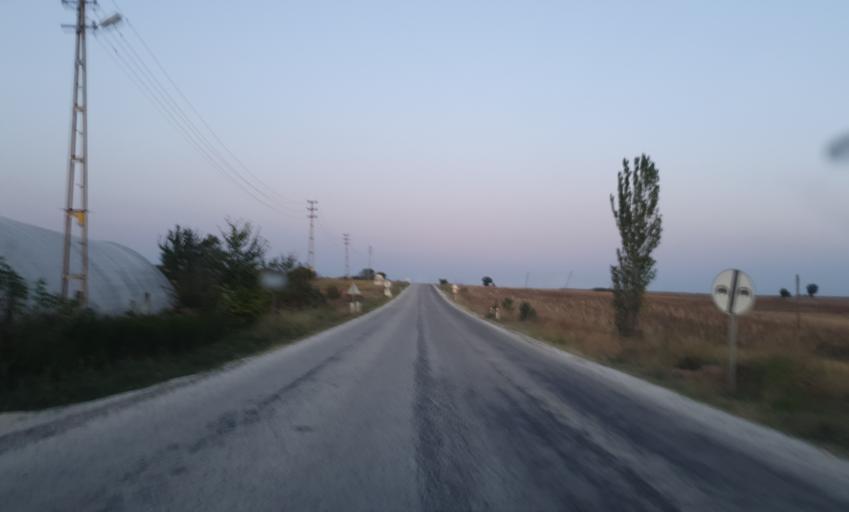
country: TR
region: Kirklareli
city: Pinarhisar
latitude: 41.6272
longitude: 27.5718
